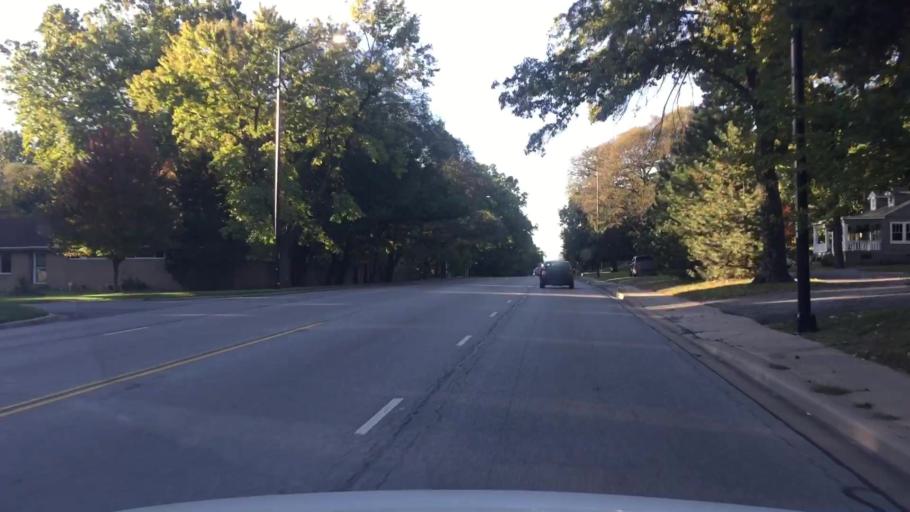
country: US
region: Kansas
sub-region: Johnson County
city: Overland Park
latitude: 39.0055
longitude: -94.6678
